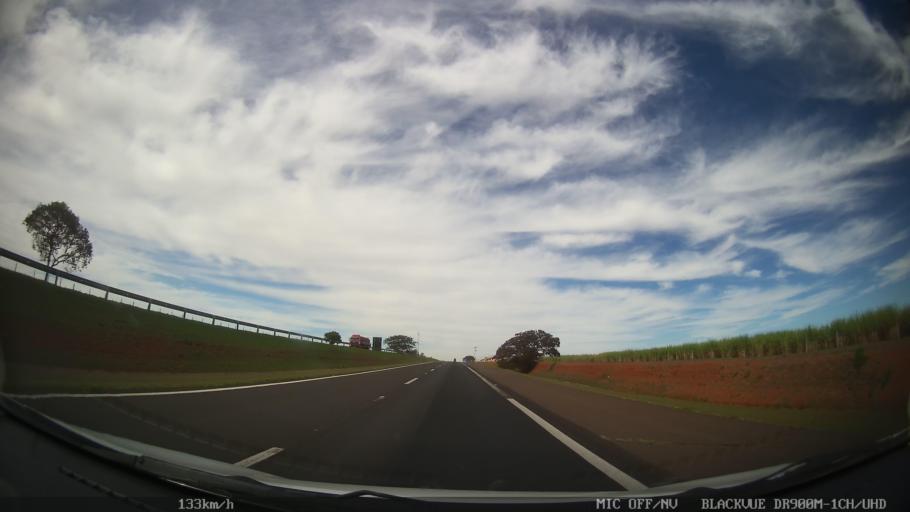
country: BR
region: Sao Paulo
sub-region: Taquaritinga
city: Taquaritinga
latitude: -21.4807
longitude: -48.5914
